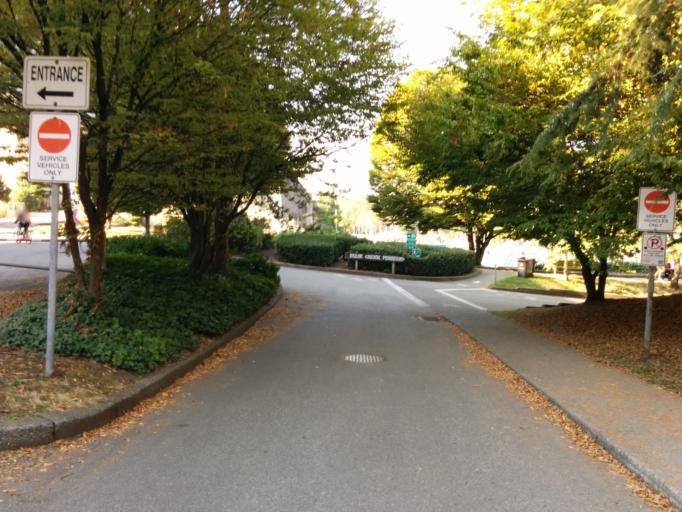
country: CA
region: British Columbia
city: West End
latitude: 49.2764
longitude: -123.1353
